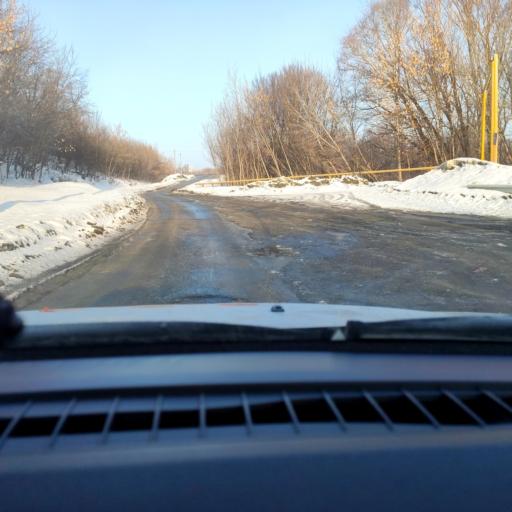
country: RU
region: Samara
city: Novokuybyshevsk
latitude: 53.1202
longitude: 49.9449
